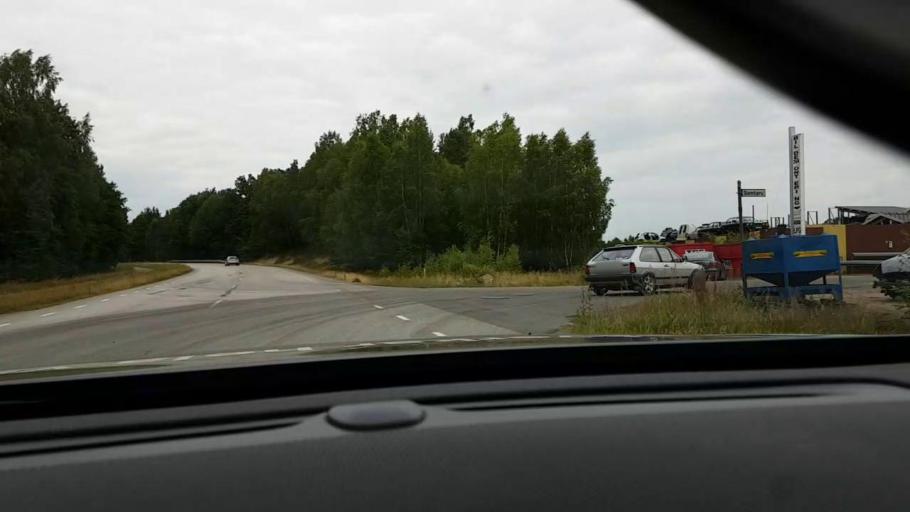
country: SE
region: Skane
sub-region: Hassleholms Kommun
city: Hassleholm
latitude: 56.1634
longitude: 13.8048
